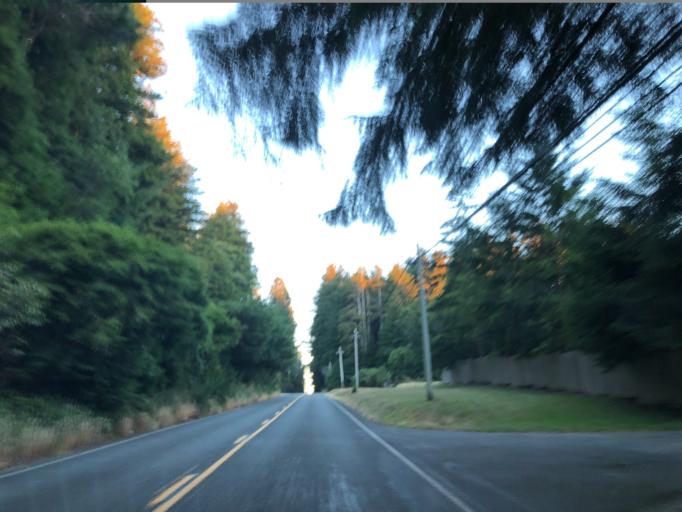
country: US
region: California
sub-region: Humboldt County
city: Westhaven-Moonstone
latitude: 41.0736
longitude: -124.1449
